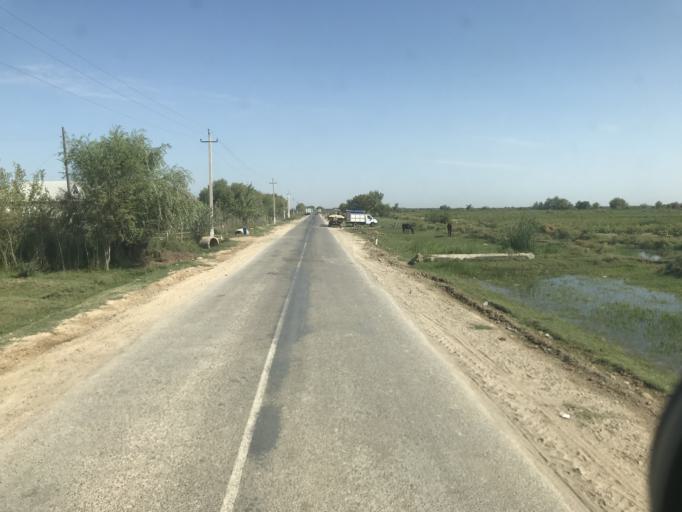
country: KZ
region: Ongtustik Qazaqstan
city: Myrzakent
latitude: 40.6648
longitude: 68.6332
